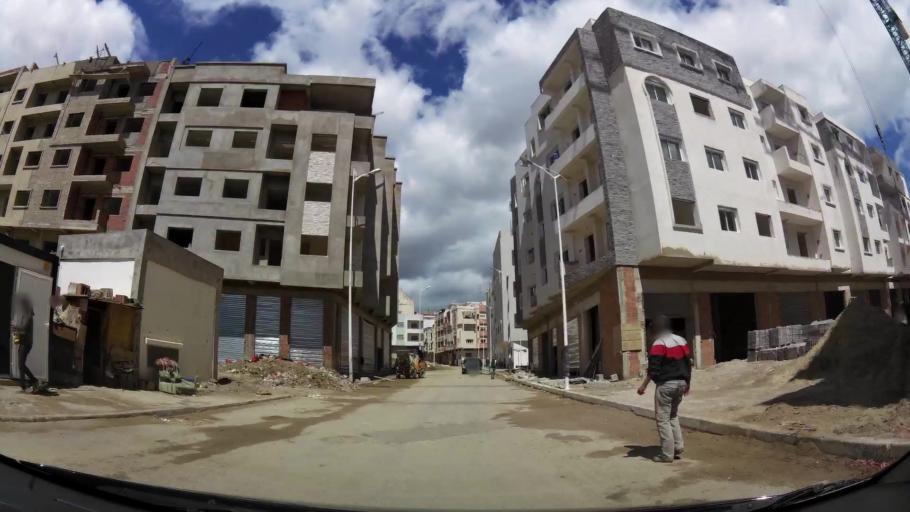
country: MA
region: Tanger-Tetouan
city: Tetouan
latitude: 35.5814
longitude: -5.3408
